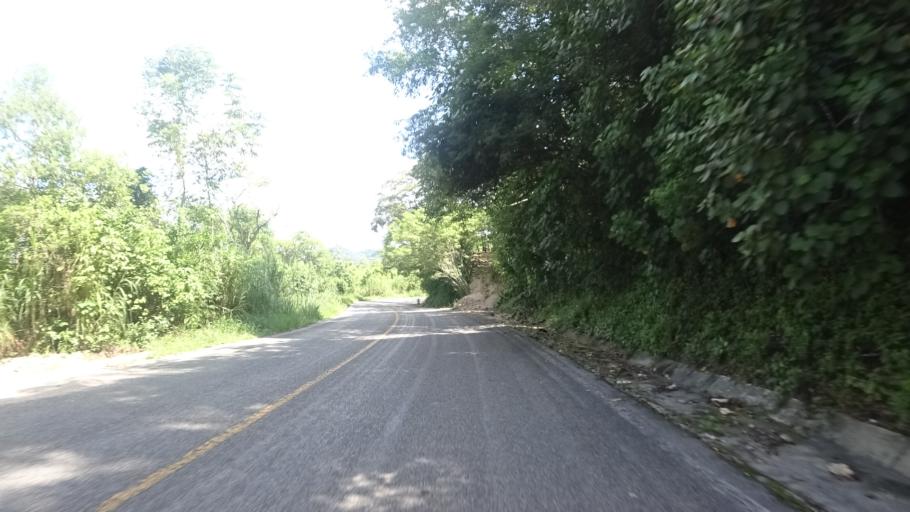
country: MX
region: Chiapas
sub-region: Palenque
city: Doctor Samuel Leon Brindis
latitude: 17.4439
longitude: -91.9686
